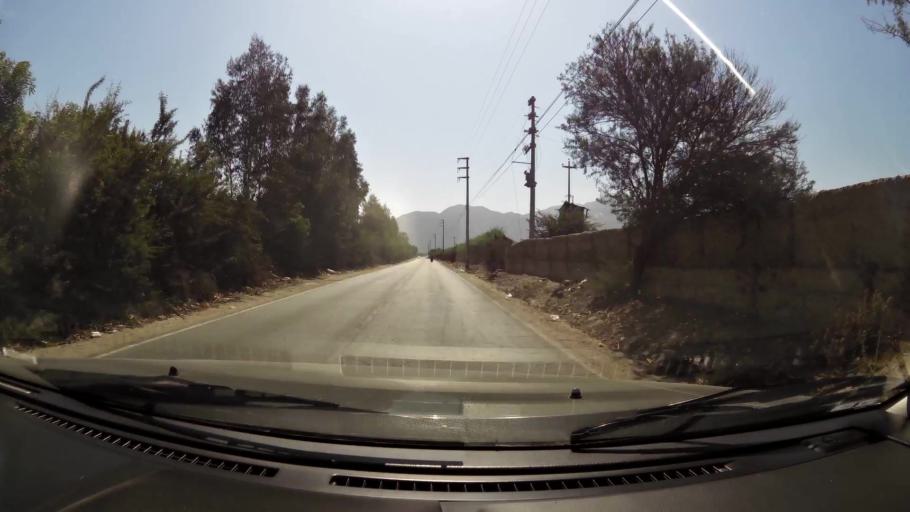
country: PE
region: Ica
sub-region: Provincia de Ica
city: San Juan Bautista
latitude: -13.9945
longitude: -75.6988
